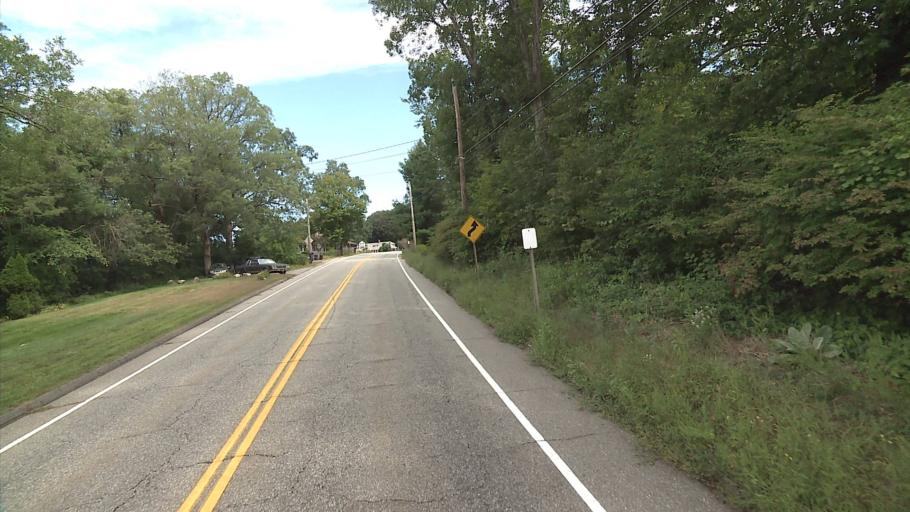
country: US
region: Connecticut
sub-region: Tolland County
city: South Coventry
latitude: 41.7825
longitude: -72.2765
